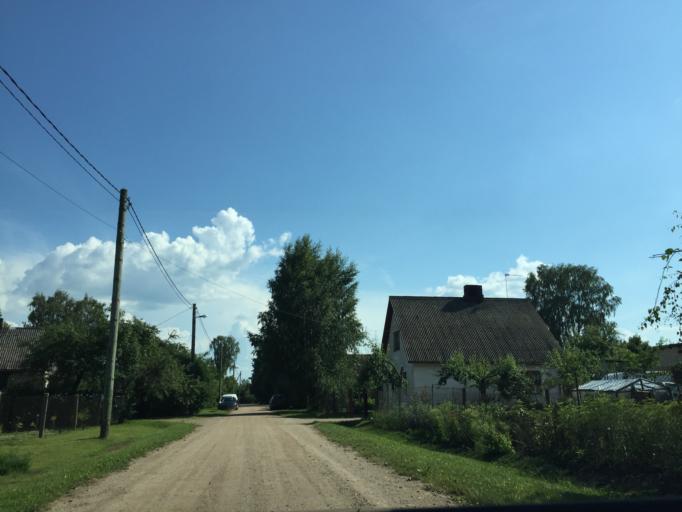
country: LV
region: Sigulda
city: Sigulda
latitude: 57.1533
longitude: 24.8673
